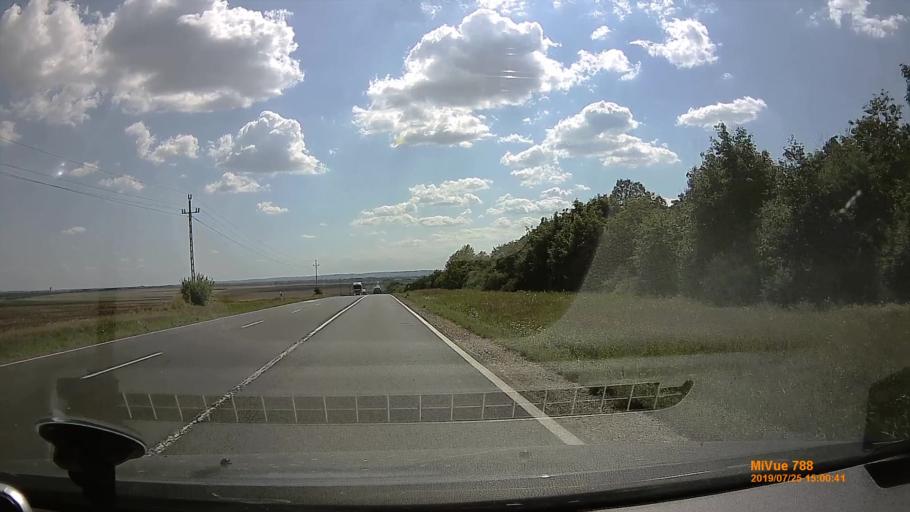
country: HU
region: Borsod-Abauj-Zemplen
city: Onga
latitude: 48.1508
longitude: 20.8950
